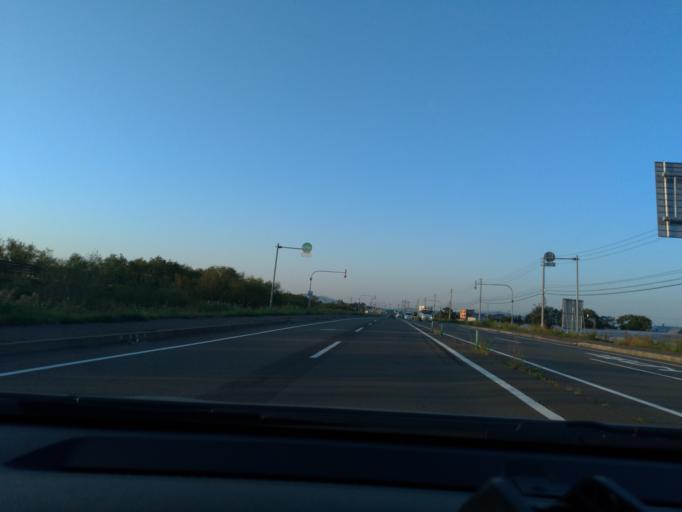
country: JP
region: Hokkaido
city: Tobetsu
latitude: 43.1861
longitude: 141.5239
